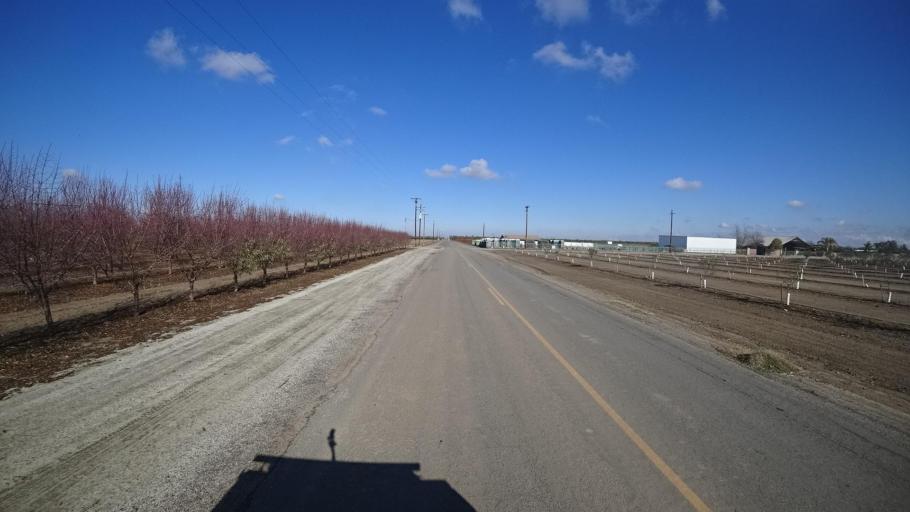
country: US
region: California
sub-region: Kern County
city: McFarland
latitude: 35.6664
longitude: -119.2588
